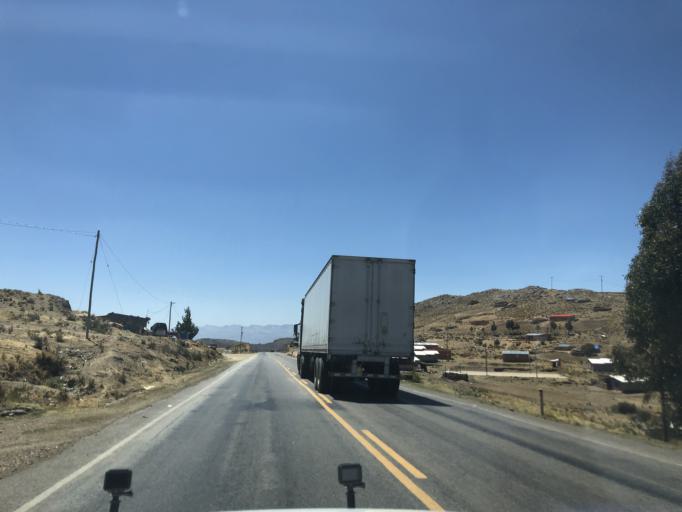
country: BO
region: Cochabamba
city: Irpa Irpa
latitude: -17.6651
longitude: -66.4817
